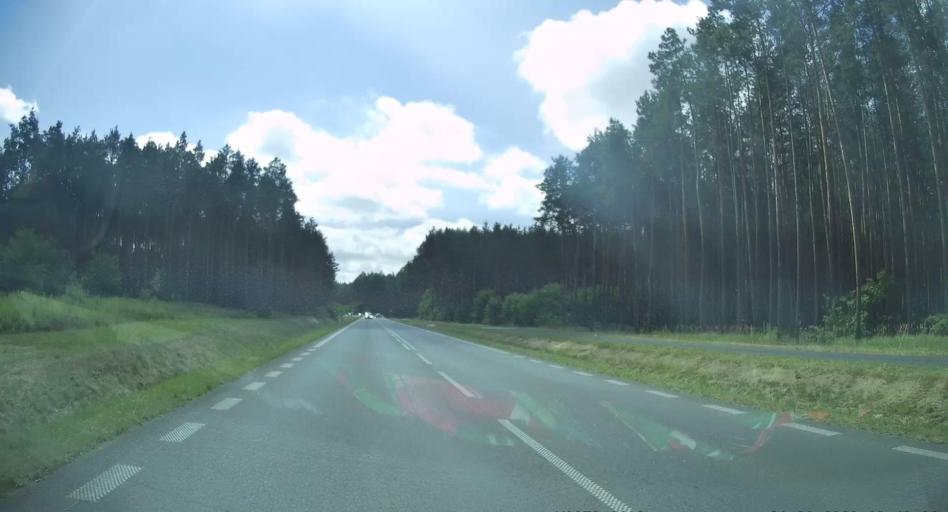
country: PL
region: Subcarpathian Voivodeship
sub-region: Powiat mielecki
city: Padew Narodowa
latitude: 50.3618
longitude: 21.4832
